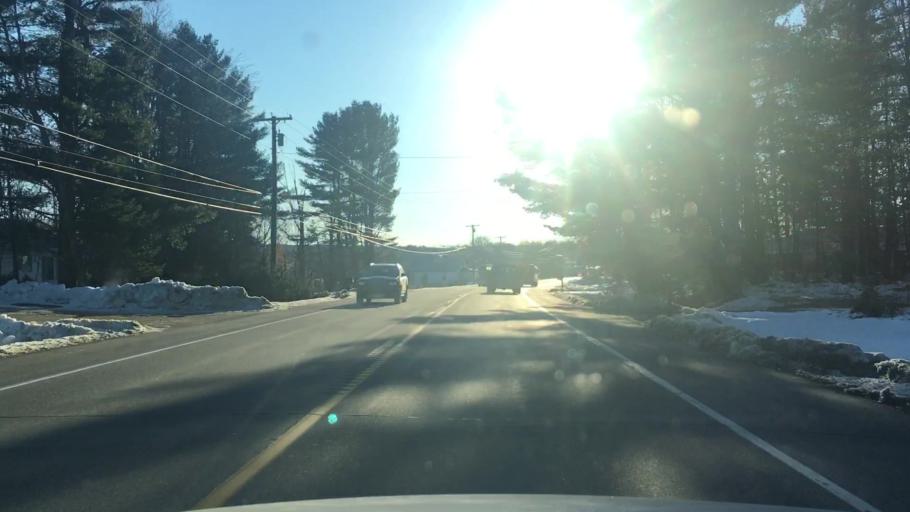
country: US
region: Maine
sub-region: Somerset County
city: Skowhegan
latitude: 44.7465
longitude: -69.7414
